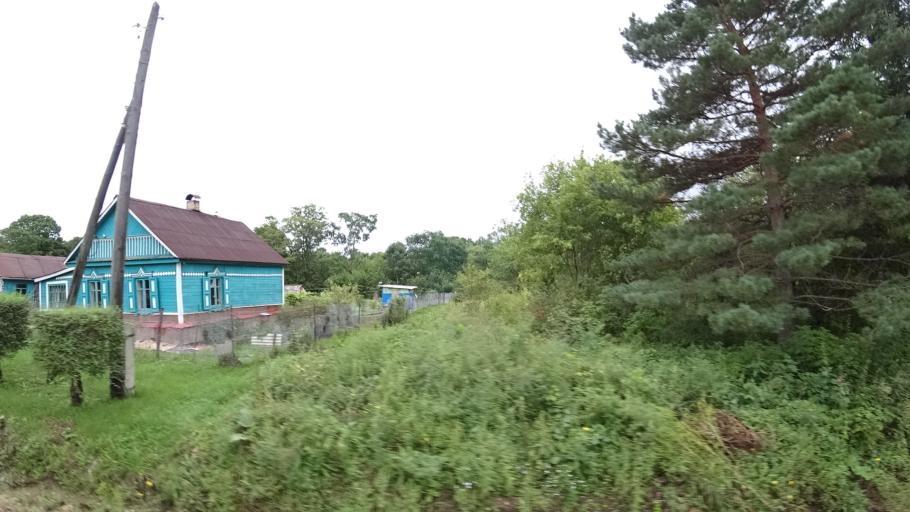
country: RU
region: Primorskiy
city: Rettikhovka
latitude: 44.1708
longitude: 132.7639
